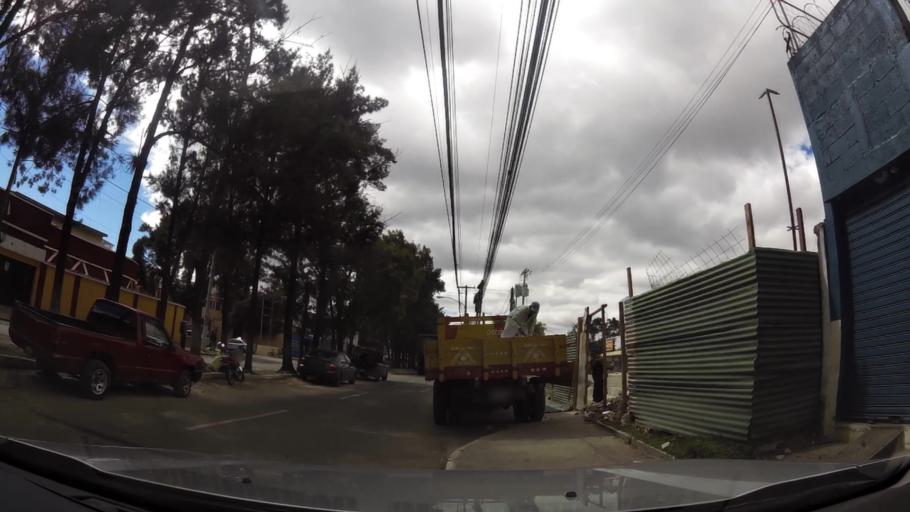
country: GT
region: Guatemala
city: Mixco
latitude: 14.6370
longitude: -90.5616
